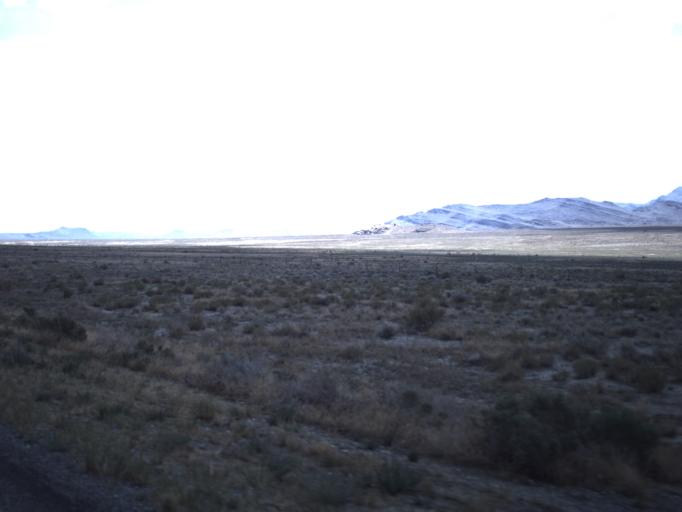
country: US
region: Utah
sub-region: Beaver County
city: Milford
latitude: 39.0446
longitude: -113.4083
